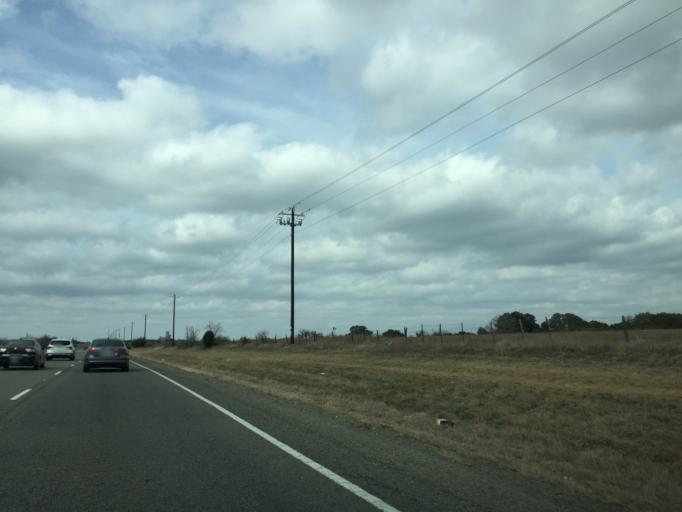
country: US
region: Texas
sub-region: Travis County
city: Briarcliff
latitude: 30.4690
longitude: -98.1737
